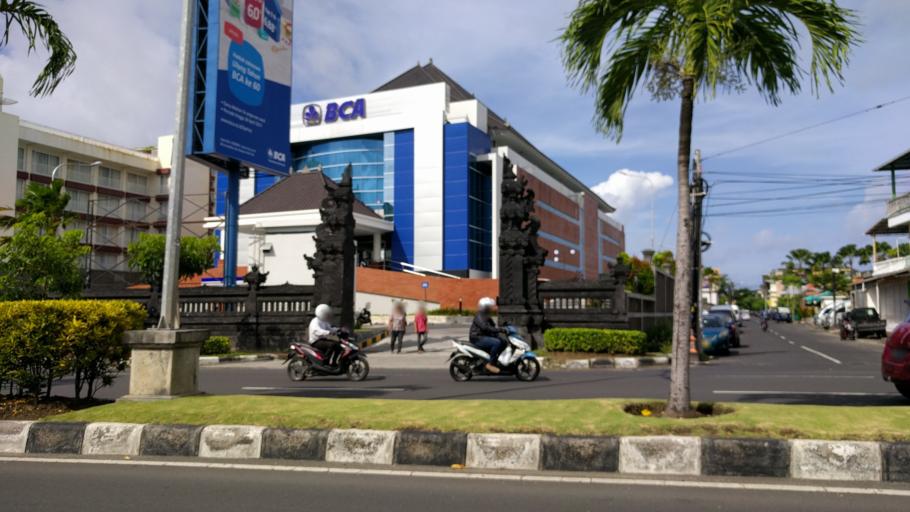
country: ID
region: Bali
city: Kuta
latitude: -8.7030
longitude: 115.1805
